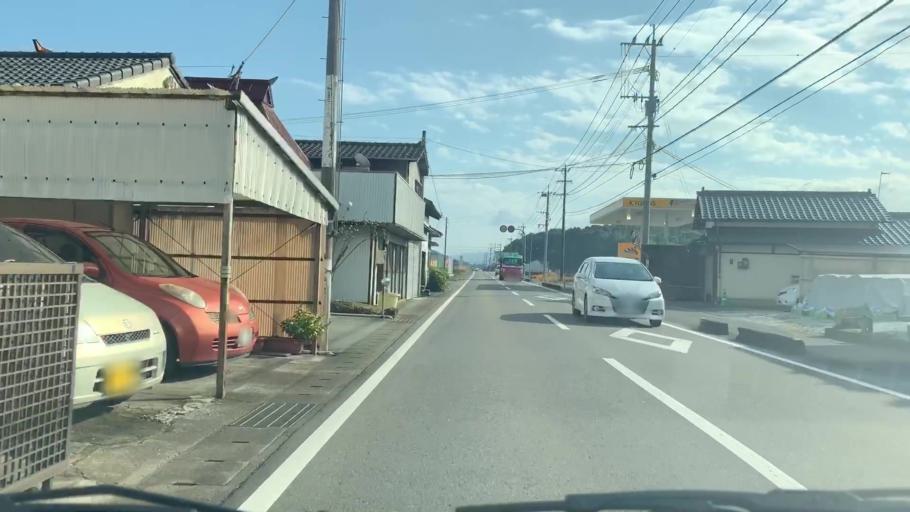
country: JP
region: Saga Prefecture
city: Takeocho-takeo
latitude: 33.1565
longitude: 130.0631
